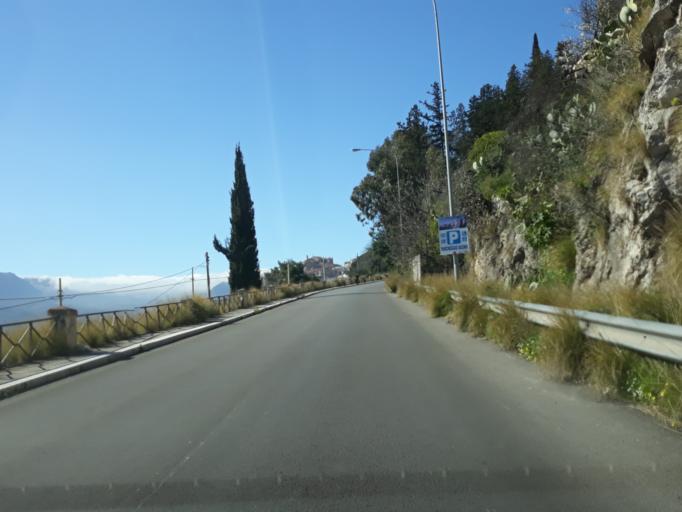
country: IT
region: Sicily
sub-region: Palermo
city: Monreale
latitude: 38.0890
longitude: 13.2998
